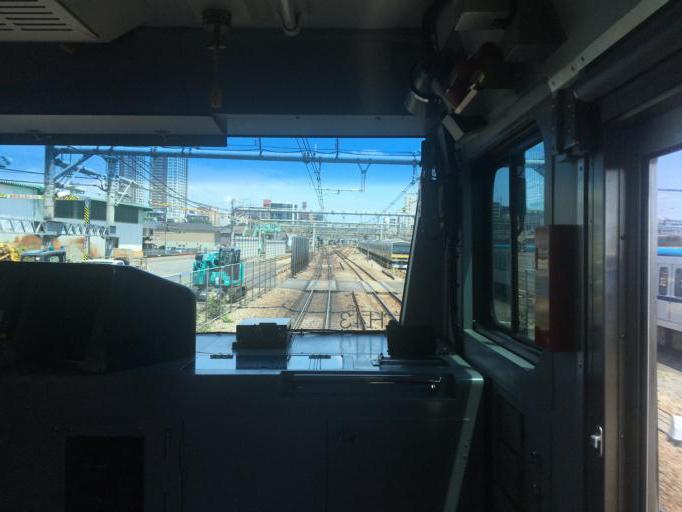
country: JP
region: Tokyo
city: Kamirenjaku
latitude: 35.7025
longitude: 139.5539
